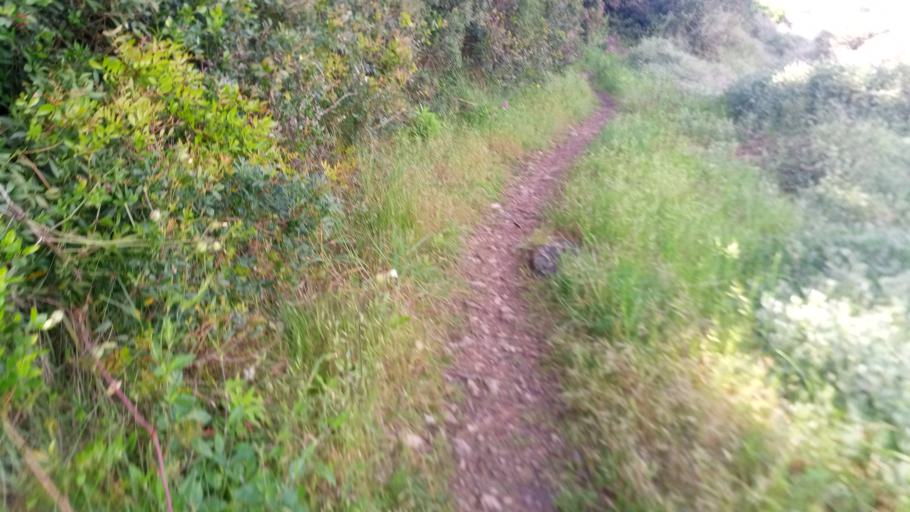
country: PT
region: Leiria
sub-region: Caldas da Rainha
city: Caldas da Rainha
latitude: 39.4024
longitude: -9.1902
